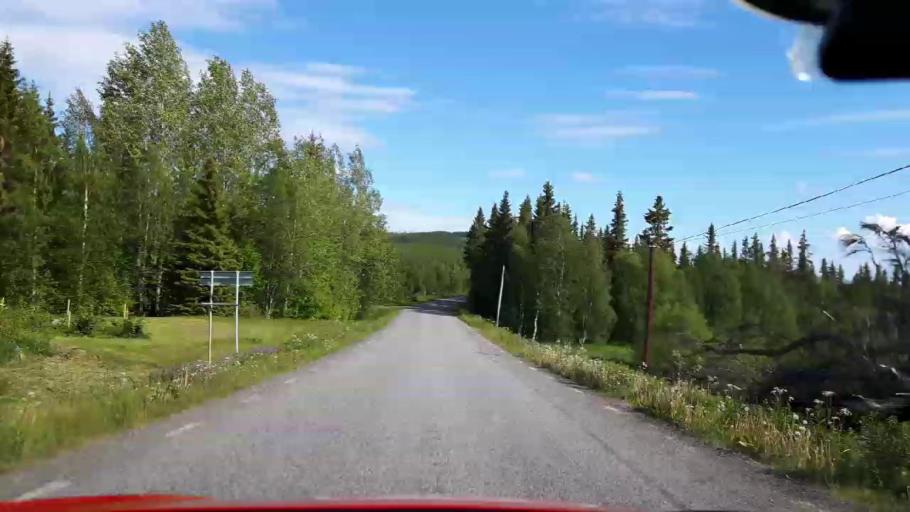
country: SE
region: Jaemtland
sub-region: Krokoms Kommun
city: Valla
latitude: 63.7578
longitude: 14.1052
